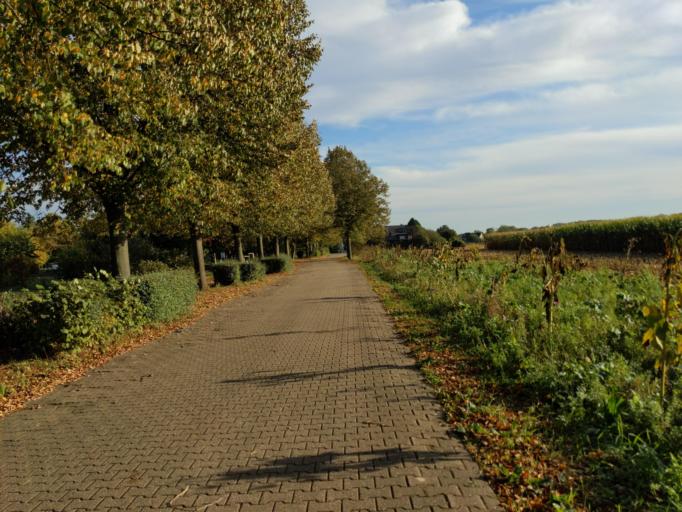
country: DE
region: North Rhine-Westphalia
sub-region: Regierungsbezirk Dusseldorf
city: Kaarst
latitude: 51.2128
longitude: 6.5860
